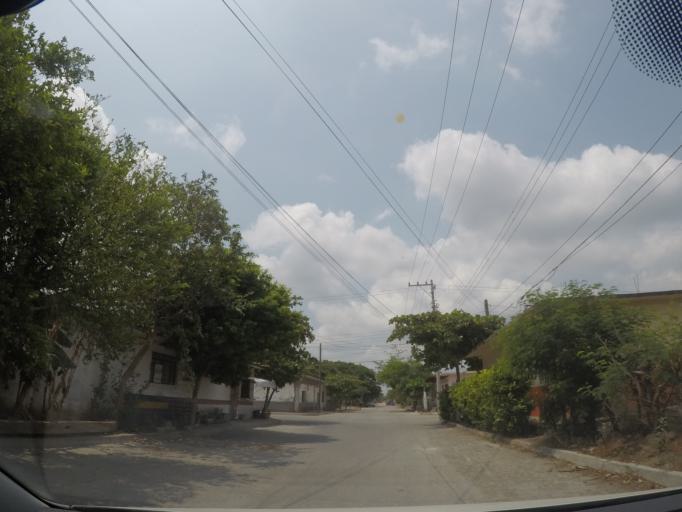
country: MX
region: Oaxaca
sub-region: El Espinal
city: El Espinal
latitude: 16.4785
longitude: -95.0428
